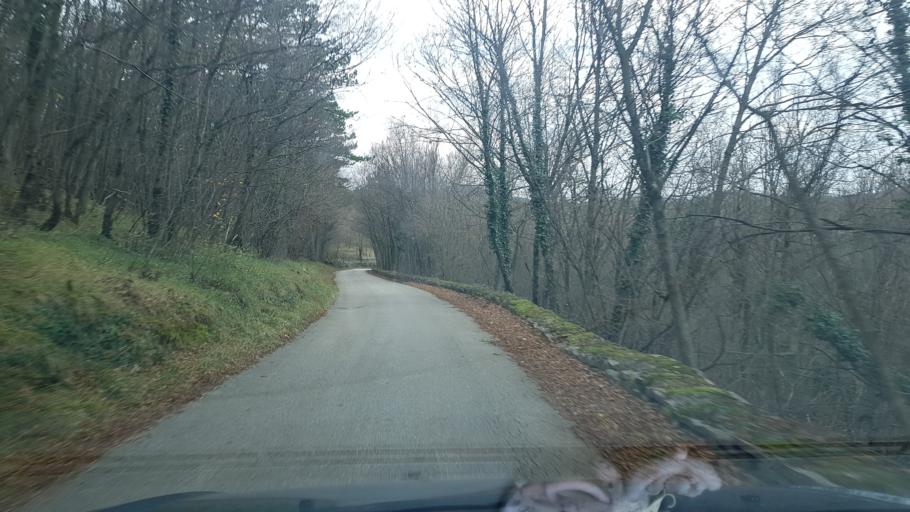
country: IT
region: Friuli Venezia Giulia
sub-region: Provincia di Trieste
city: Zolla
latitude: 45.7216
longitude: 13.8013
